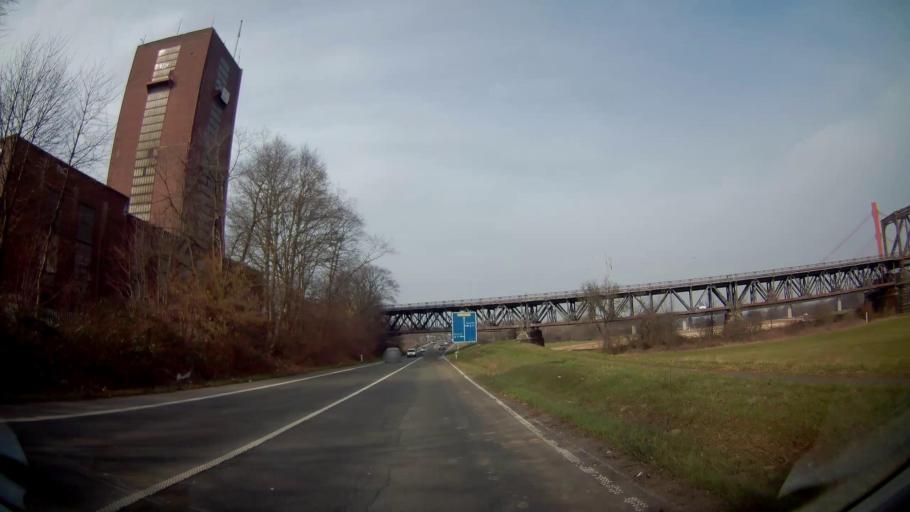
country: DE
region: North Rhine-Westphalia
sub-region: Regierungsbezirk Dusseldorf
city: Moers
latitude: 51.4771
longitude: 6.6770
